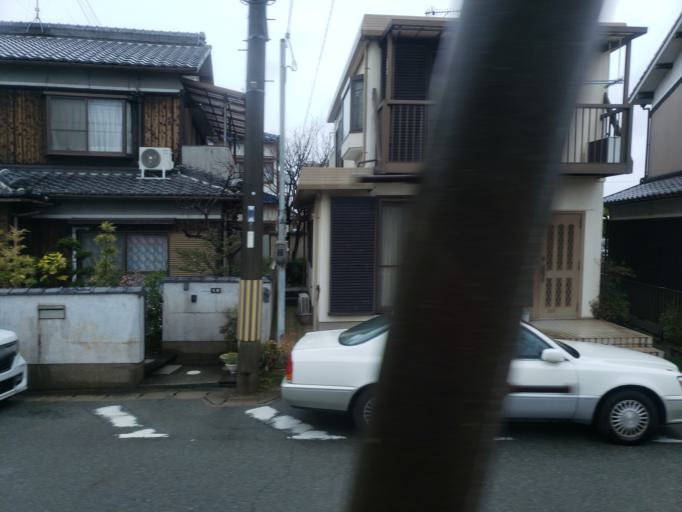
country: JP
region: Hyogo
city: Kakogawacho-honmachi
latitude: 34.7145
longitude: 134.8701
